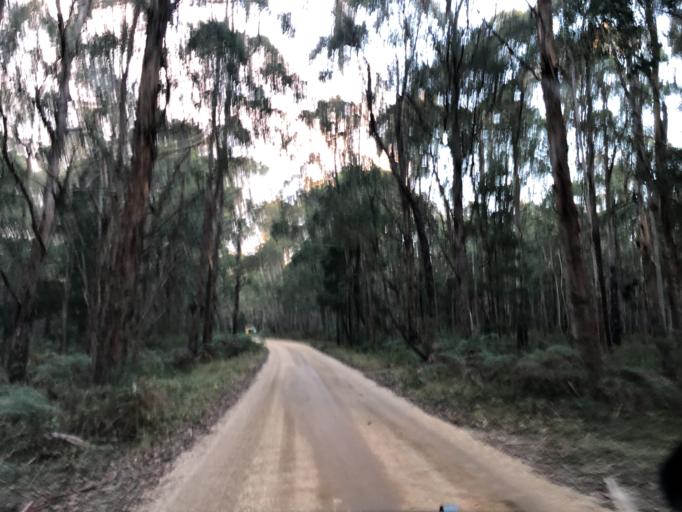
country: AU
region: Victoria
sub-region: Moorabool
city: Bacchus Marsh
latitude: -37.4155
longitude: 144.3965
